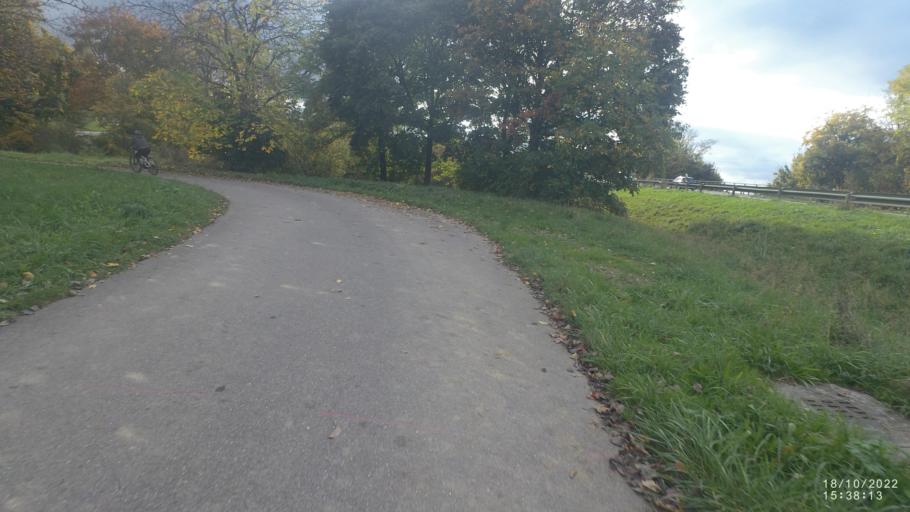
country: DE
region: Baden-Wuerttemberg
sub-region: Regierungsbezirk Stuttgart
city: Aichelberg
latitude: 48.6400
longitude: 9.5608
